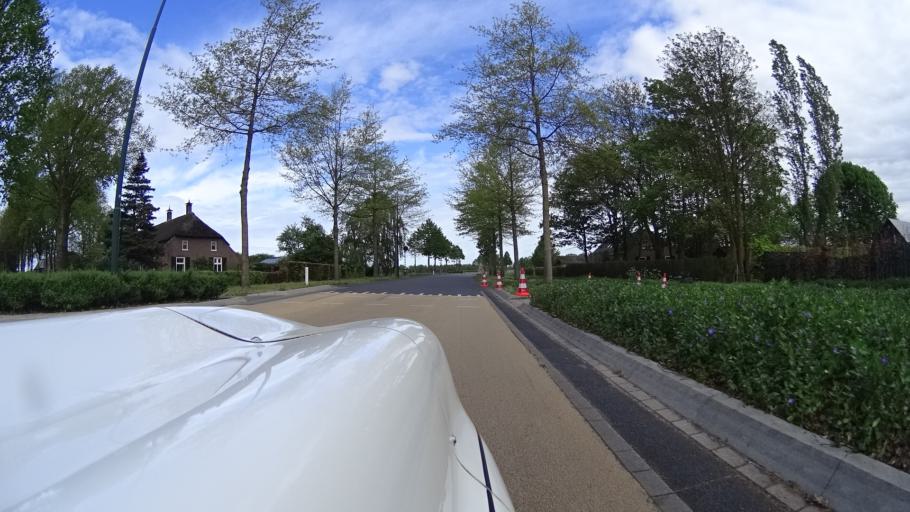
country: NL
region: North Brabant
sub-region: Gemeente Sint Anthonis
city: Sint Anthonis
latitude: 51.6064
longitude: 5.8686
